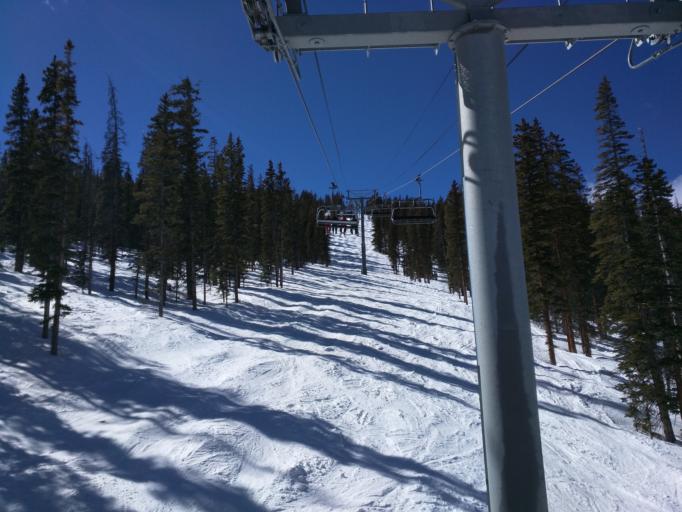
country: US
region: Colorado
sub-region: Grand County
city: Fraser
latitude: 39.8508
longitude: -105.7661
